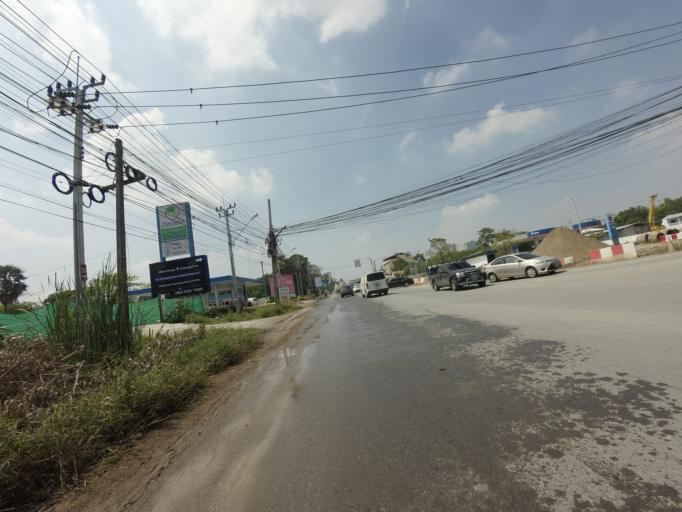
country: TH
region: Bangkok
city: Suan Luang
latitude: 13.7477
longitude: 100.6567
